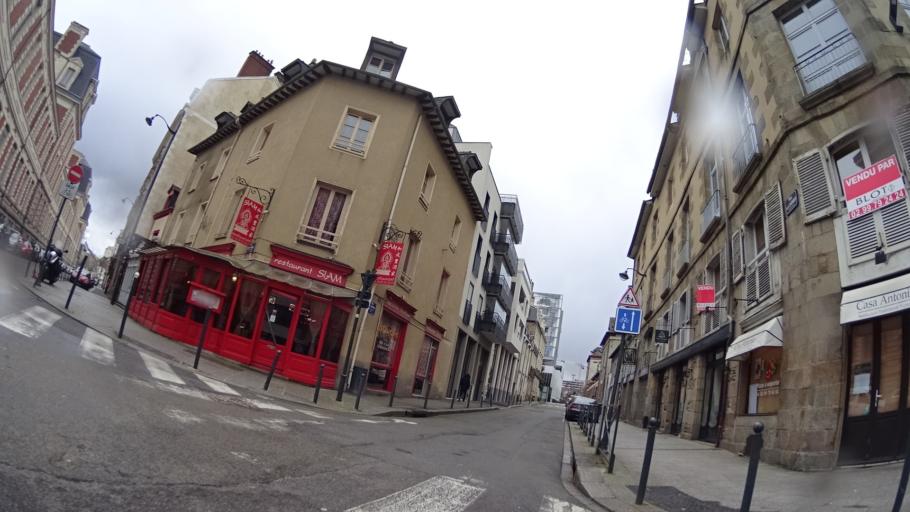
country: FR
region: Brittany
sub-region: Departement d'Ille-et-Vilaine
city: Rennes
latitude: 48.1085
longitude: -1.6762
